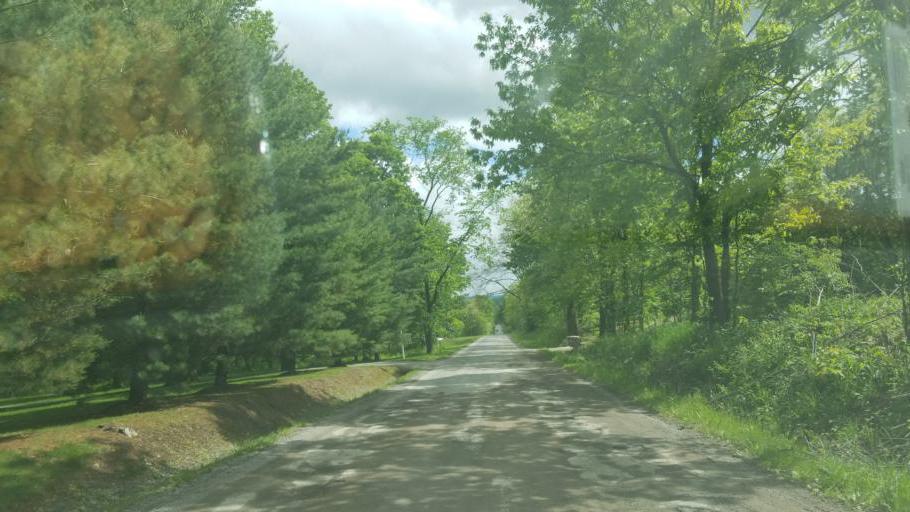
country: US
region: Ohio
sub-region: Geauga County
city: Middlefield
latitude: 41.4348
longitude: -81.0033
